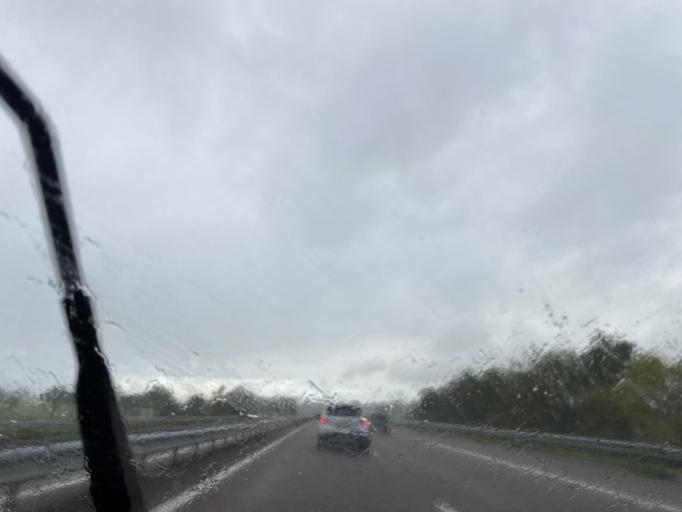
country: FR
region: Auvergne
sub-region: Departement de l'Allier
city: Estivareilles
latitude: 46.4398
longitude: 2.6949
